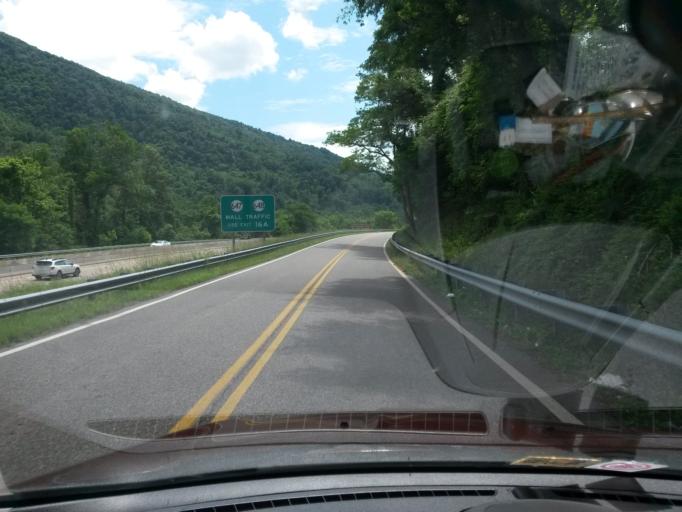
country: US
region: Virginia
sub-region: City of Covington
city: Fairlawn
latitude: 37.7774
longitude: -79.9363
